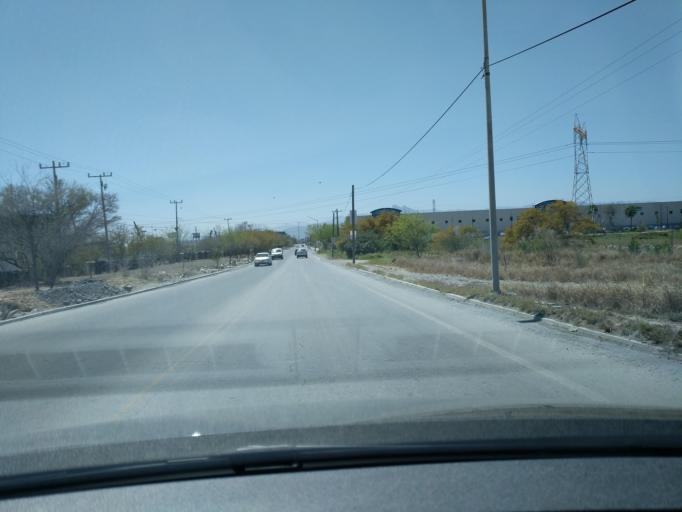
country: MX
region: Nuevo Leon
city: Apodaca
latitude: 25.7921
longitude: -100.1580
